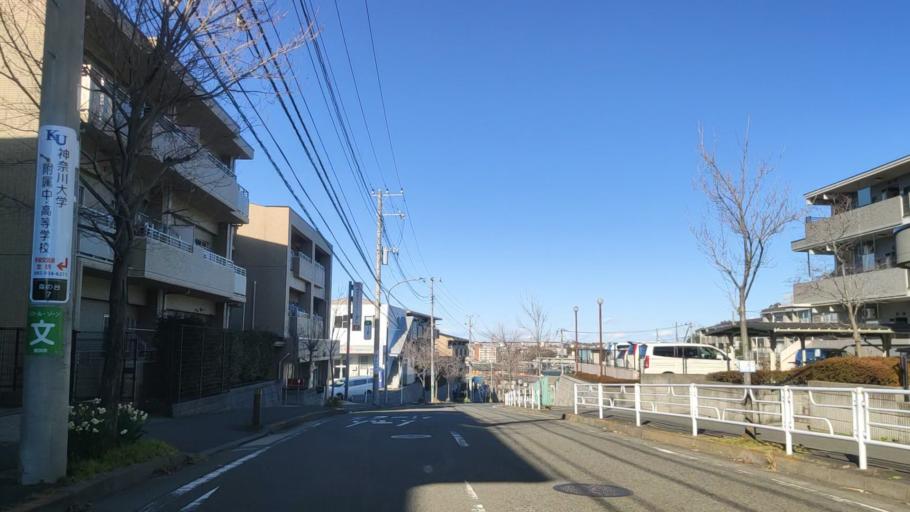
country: JP
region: Kanagawa
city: Minami-rinkan
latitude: 35.5088
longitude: 139.5347
